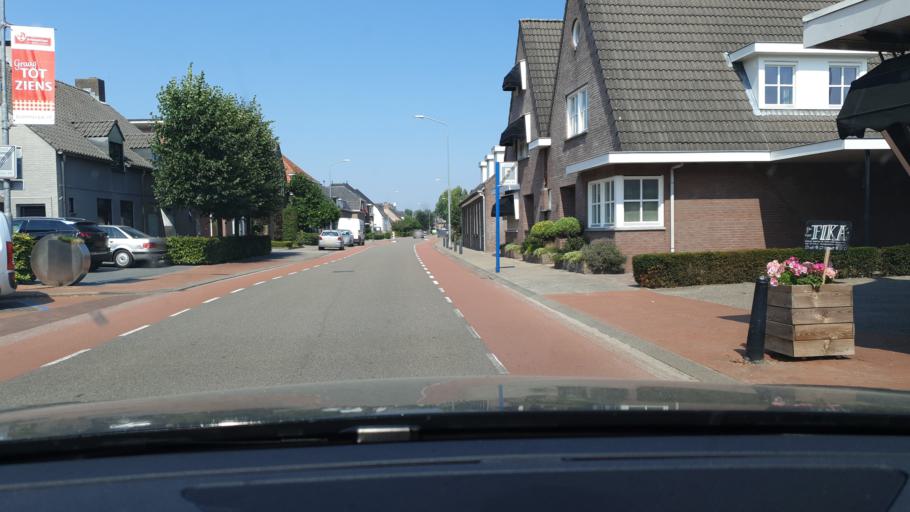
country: NL
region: North Brabant
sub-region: Gemeente Veldhoven
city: Veldhoven
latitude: 51.4038
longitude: 5.3928
